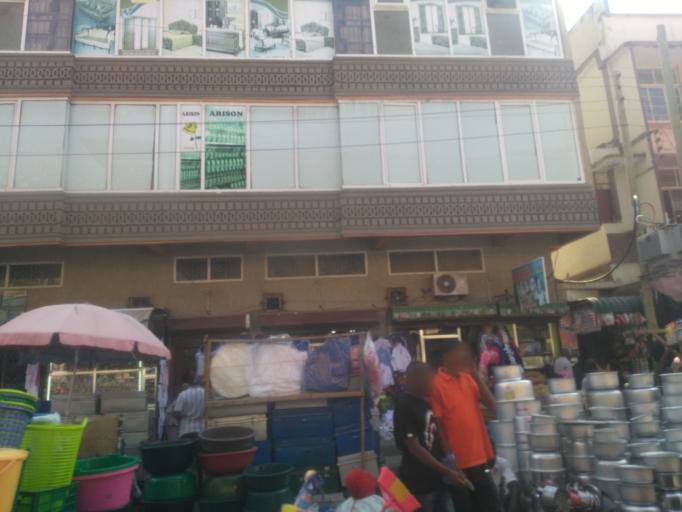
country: TZ
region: Dar es Salaam
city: Dar es Salaam
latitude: -6.8201
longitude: 39.2747
